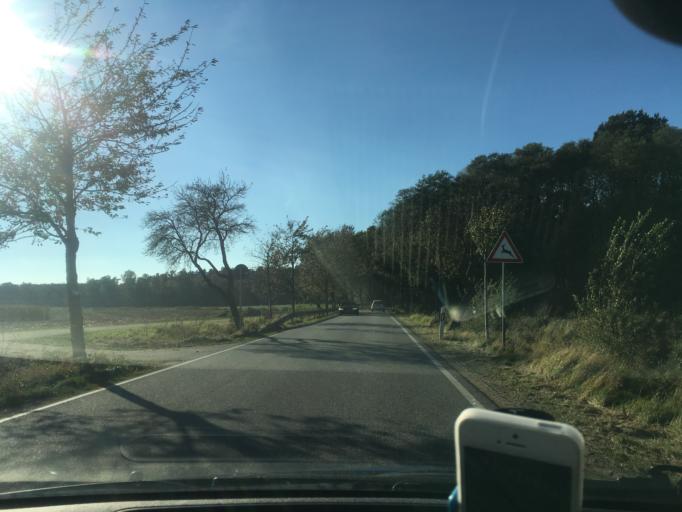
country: DE
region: Mecklenburg-Vorpommern
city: Dummer
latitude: 53.5484
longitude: 11.1721
